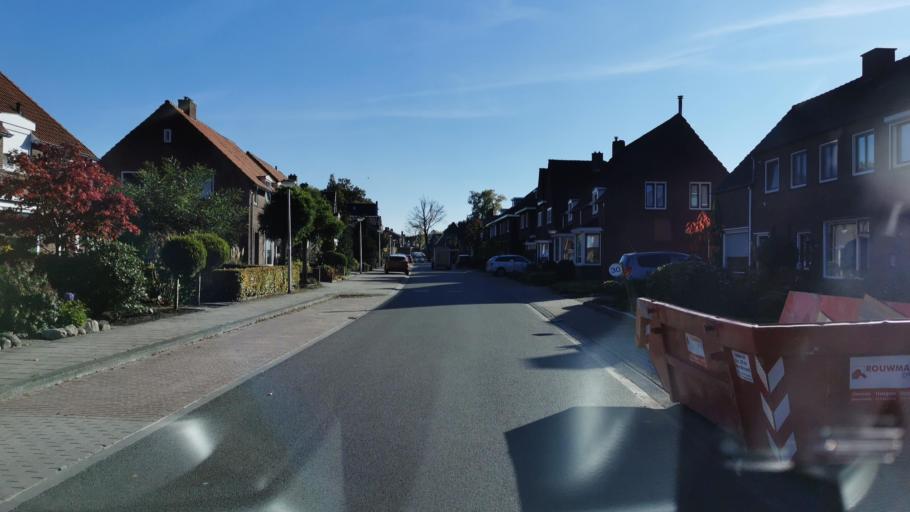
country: NL
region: Overijssel
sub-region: Gemeente Enschede
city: Enschede
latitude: 52.2513
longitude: 6.9091
